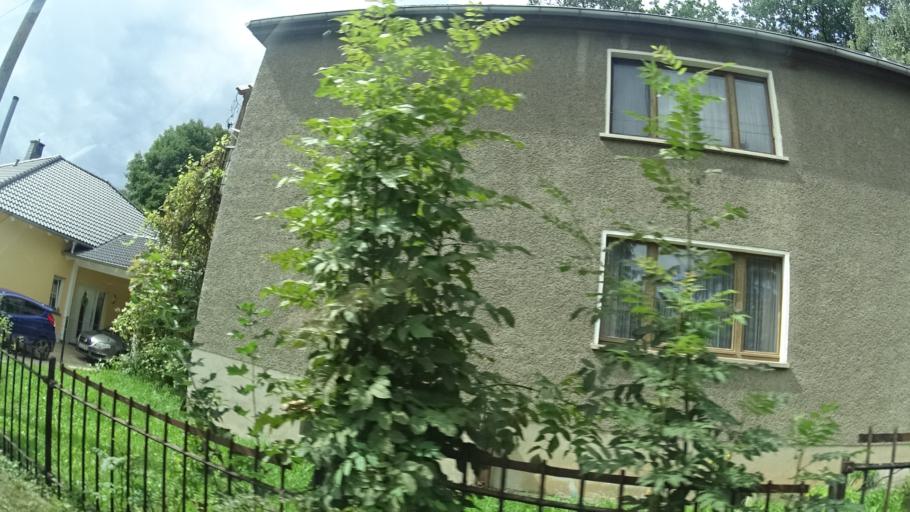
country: DE
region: Thuringia
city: Unterwellenborn
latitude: 50.6662
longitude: 11.4227
